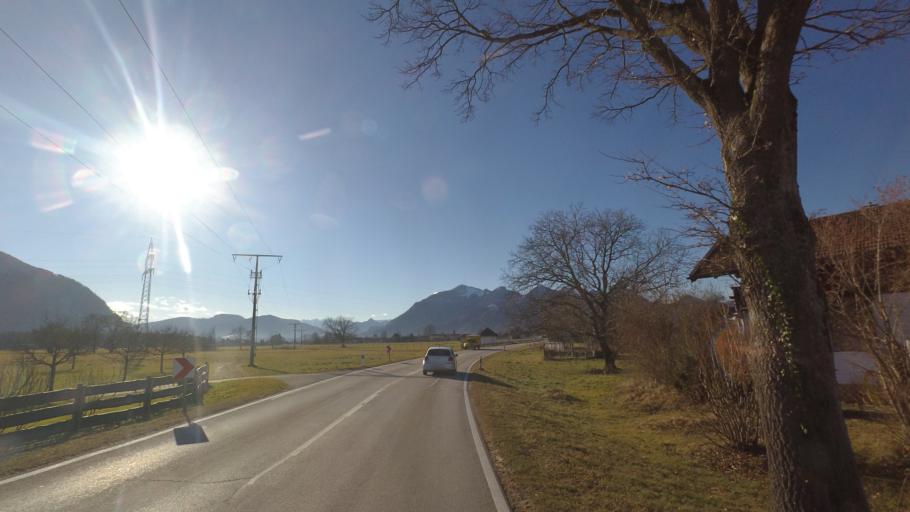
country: DE
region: Bavaria
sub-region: Upper Bavaria
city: Ubersee
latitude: 47.8020
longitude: 12.4799
